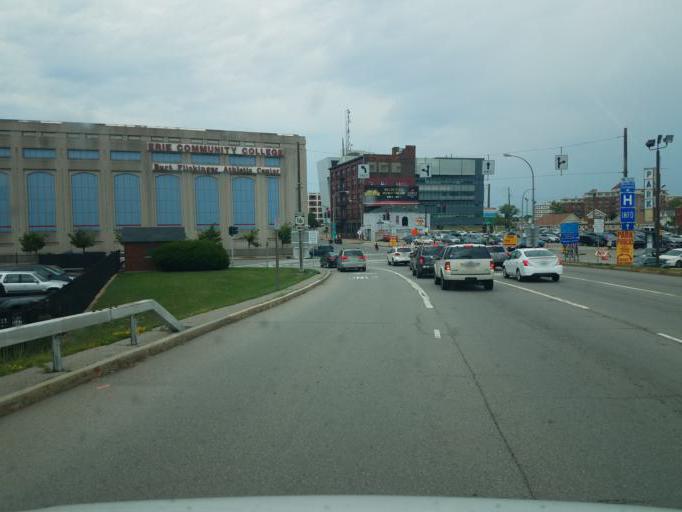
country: US
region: New York
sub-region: Erie County
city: Buffalo
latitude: 42.8806
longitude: -78.8713
